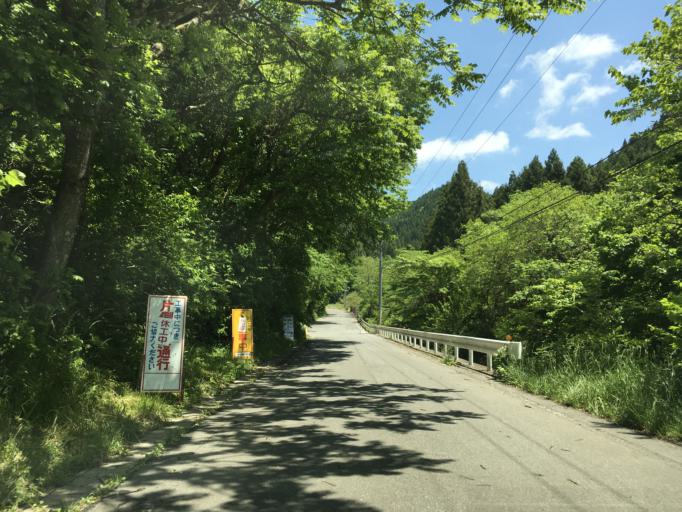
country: JP
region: Miyagi
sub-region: Oshika Gun
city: Onagawa Cho
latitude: 38.6737
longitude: 141.3495
